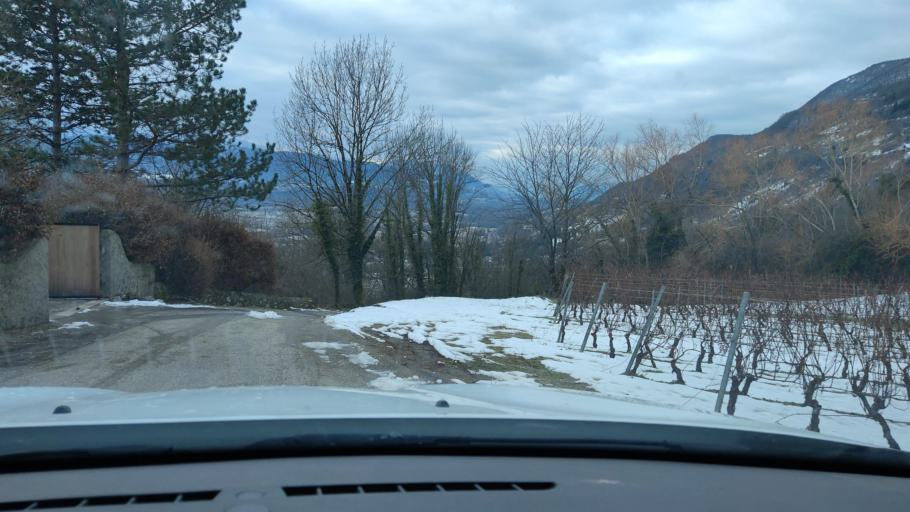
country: FR
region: Rhone-Alpes
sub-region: Departement de la Savoie
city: Coise-Saint-Jean-Pied-Gauthier
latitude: 45.5655
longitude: 6.1330
